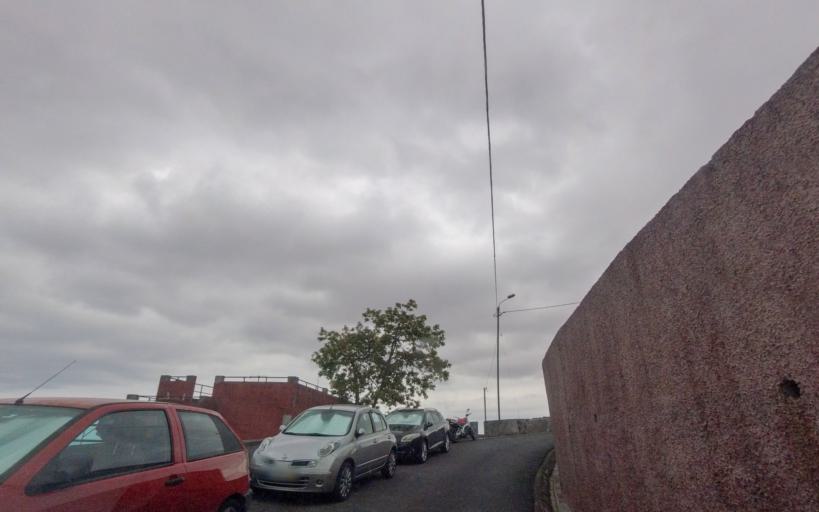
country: PT
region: Madeira
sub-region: Funchal
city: Nossa Senhora do Monte
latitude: 32.6616
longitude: -16.8886
